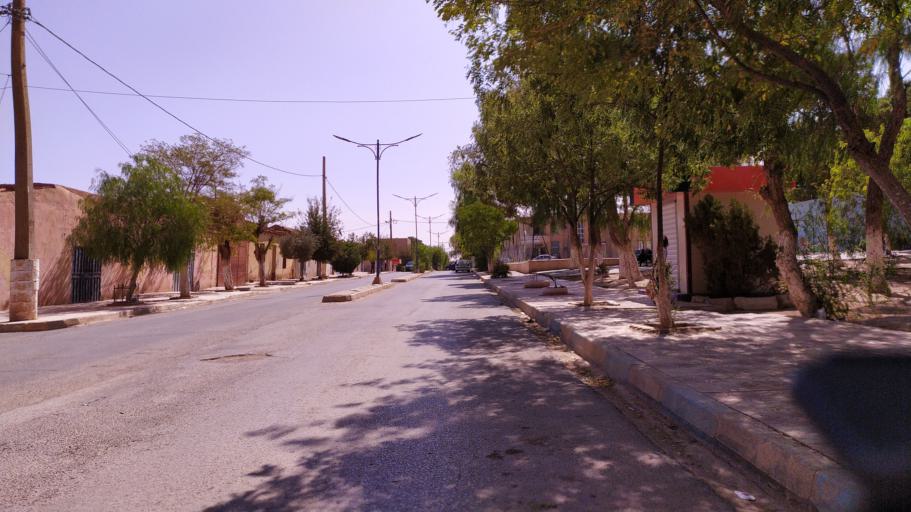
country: DZ
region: Tiaret
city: Frenda
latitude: 34.8955
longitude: 1.2415
